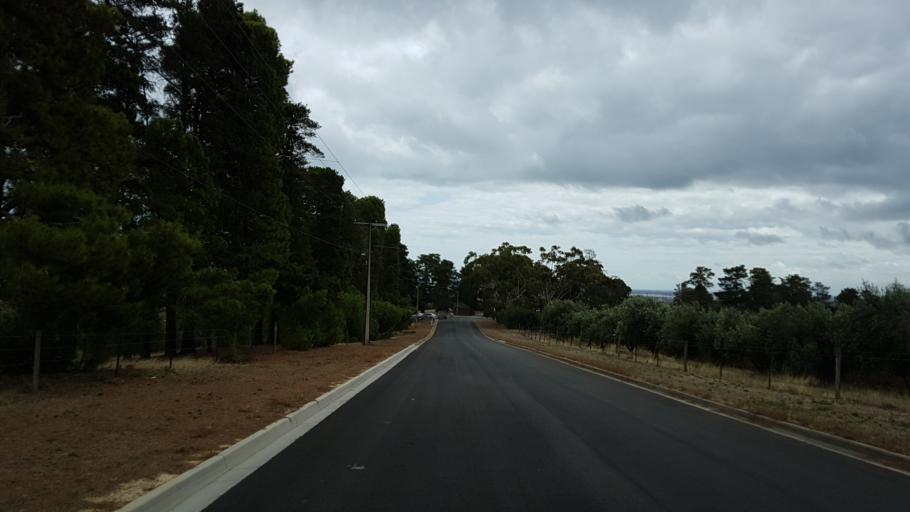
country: AU
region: South Australia
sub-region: Onkaparinga
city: Bedford Park
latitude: -35.0426
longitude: 138.5655
